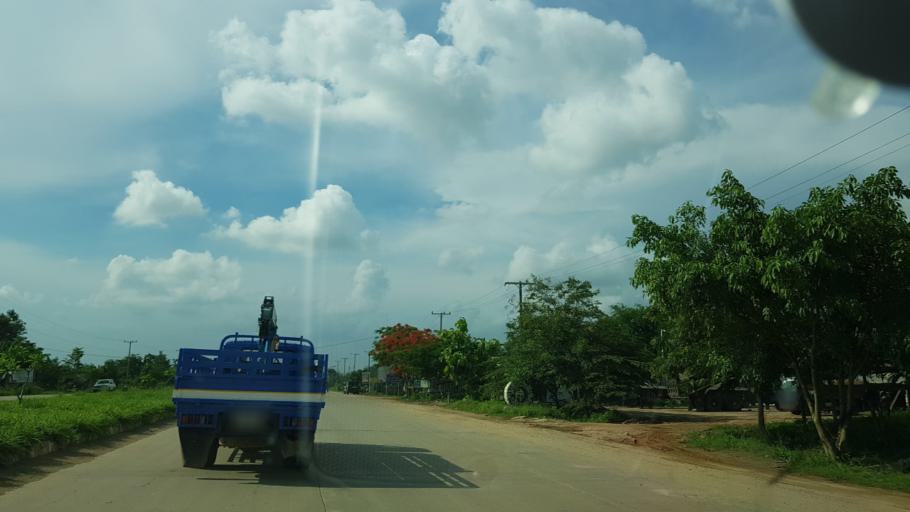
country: TH
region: Nong Khai
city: Nong Khai
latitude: 17.9127
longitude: 102.7199
